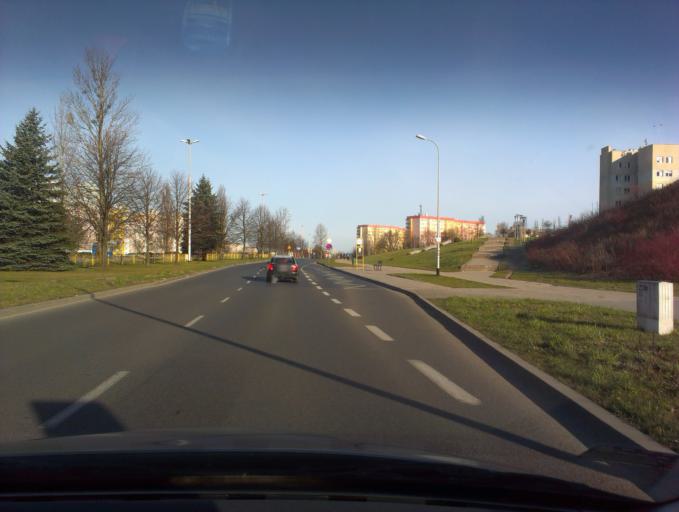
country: PL
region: West Pomeranian Voivodeship
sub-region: Koszalin
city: Koszalin
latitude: 54.2022
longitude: 16.1975
